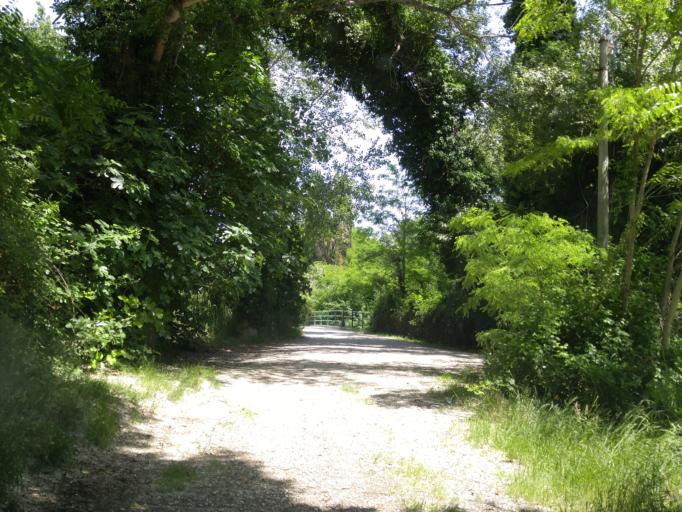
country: IT
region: The Marches
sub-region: Provincia di Pesaro e Urbino
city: Bellocchi
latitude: 43.7707
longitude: 12.9884
